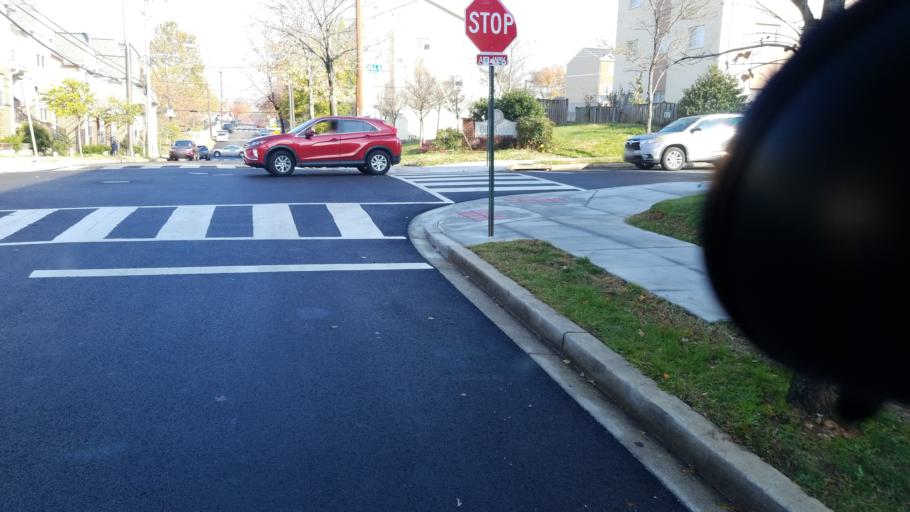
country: US
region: Maryland
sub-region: Prince George's County
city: Capitol Heights
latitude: 38.8844
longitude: -76.9309
